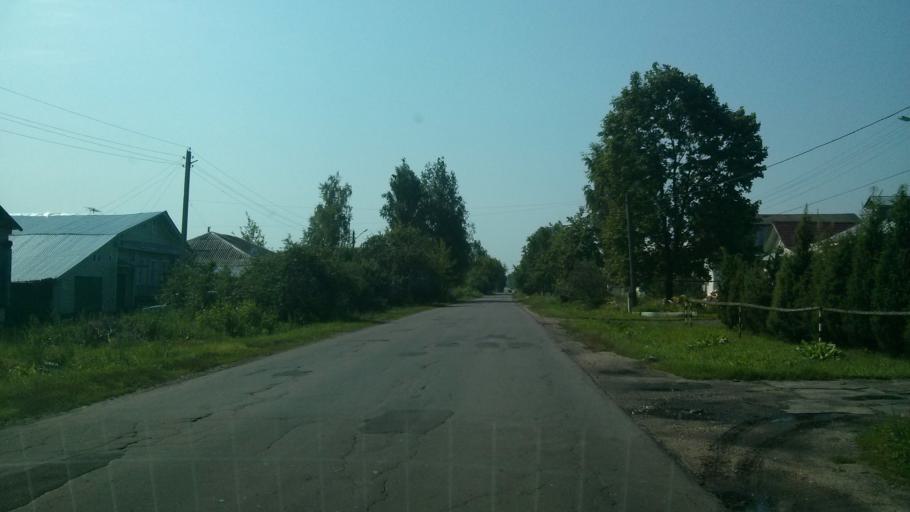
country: RU
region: Vladimir
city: Murom
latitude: 55.5410
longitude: 42.0253
